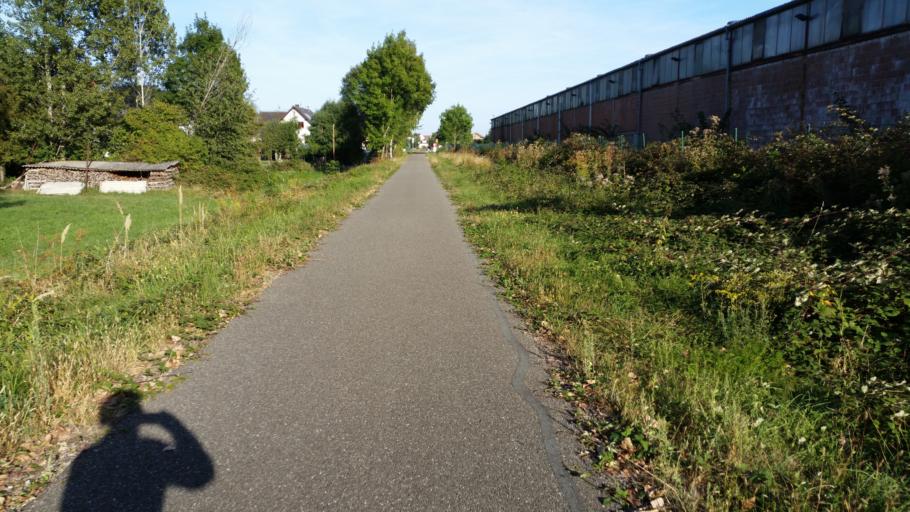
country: FR
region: Alsace
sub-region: Departement du Bas-Rhin
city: Betschdorf
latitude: 48.8964
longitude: 7.8993
